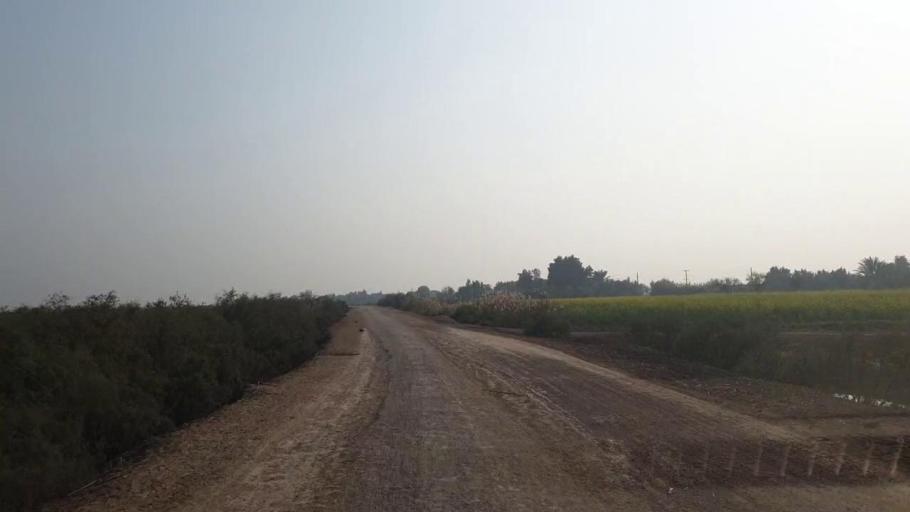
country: PK
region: Sindh
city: Shahdadpur
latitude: 25.9704
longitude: 68.5221
